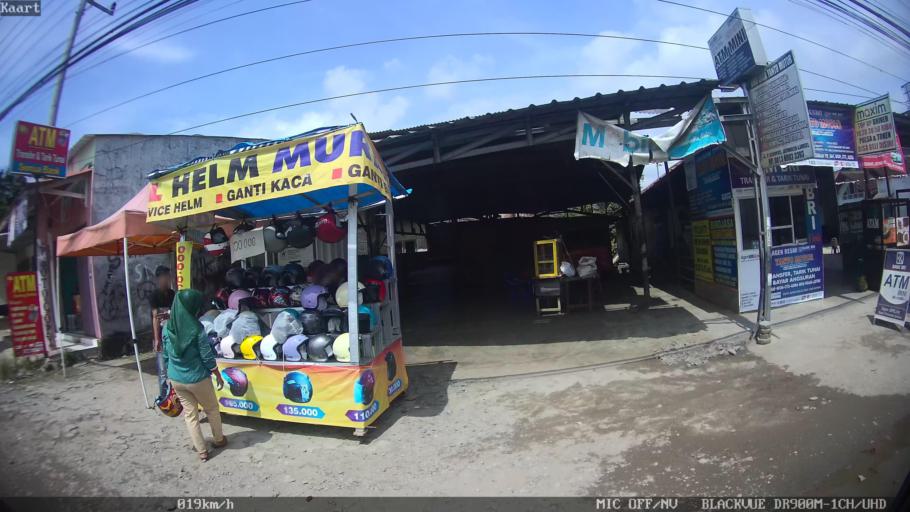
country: ID
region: Lampung
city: Kedaton
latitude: -5.3424
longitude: 105.2945
